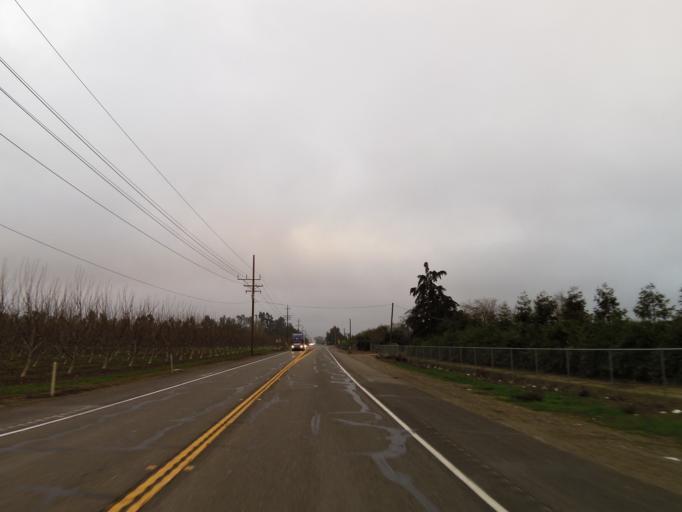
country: US
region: California
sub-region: Stanislaus County
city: Riverdale Park
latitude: 37.6383
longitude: -121.0628
